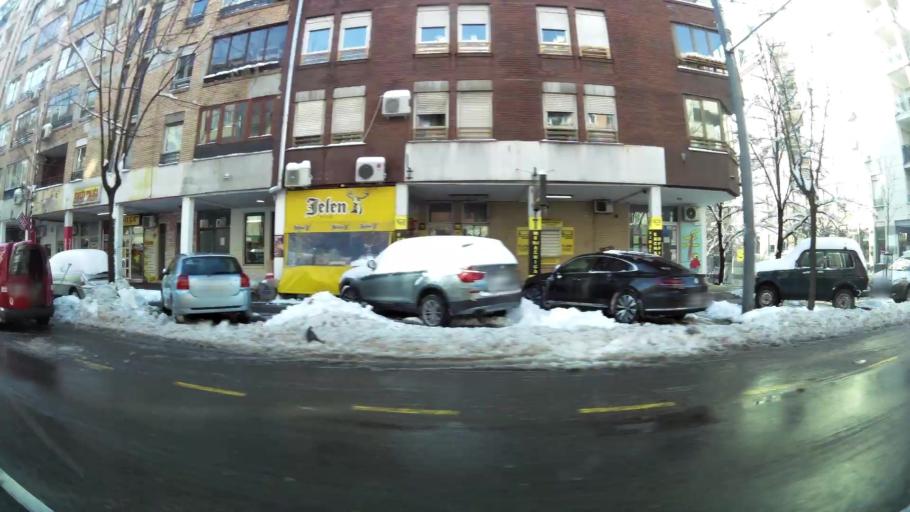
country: RS
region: Central Serbia
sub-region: Belgrade
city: Vracar
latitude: 44.7939
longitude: 20.4936
